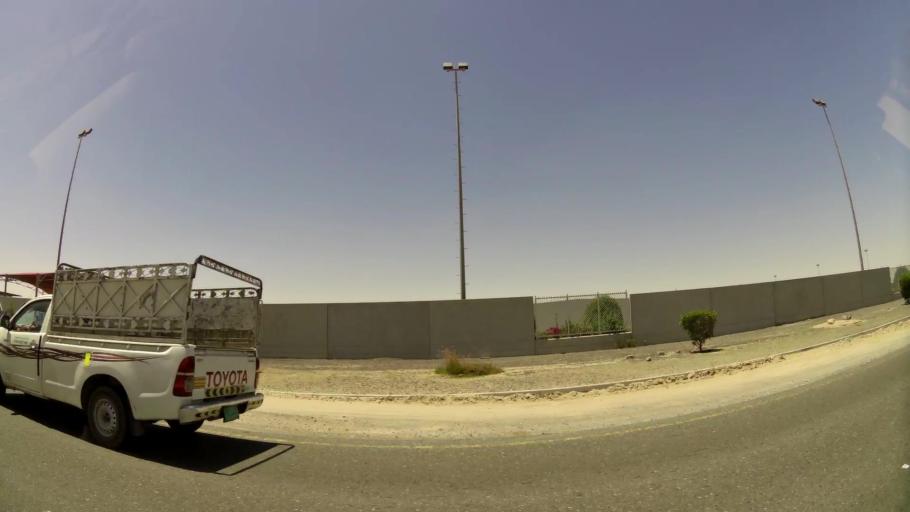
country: AE
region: Dubai
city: Dubai
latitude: 24.9658
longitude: 55.2001
